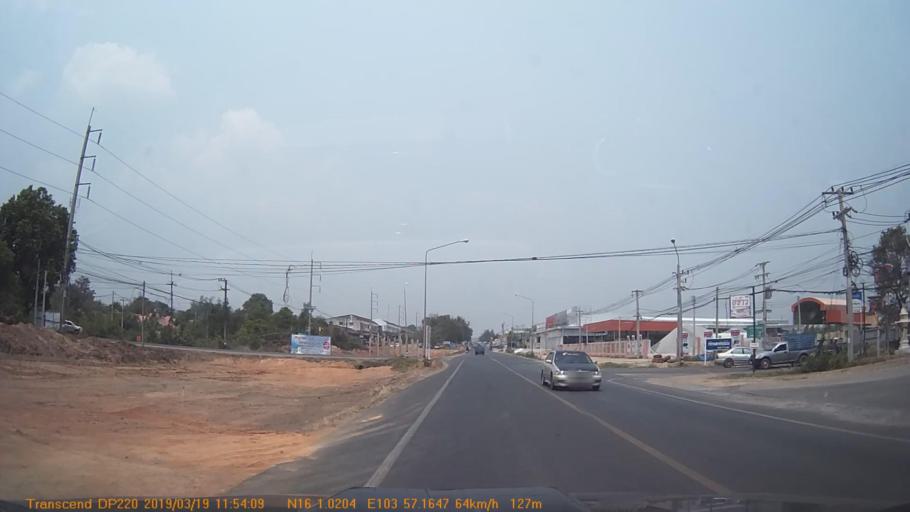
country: TH
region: Roi Et
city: Ban Selaphum
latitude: 16.0171
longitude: 103.9527
